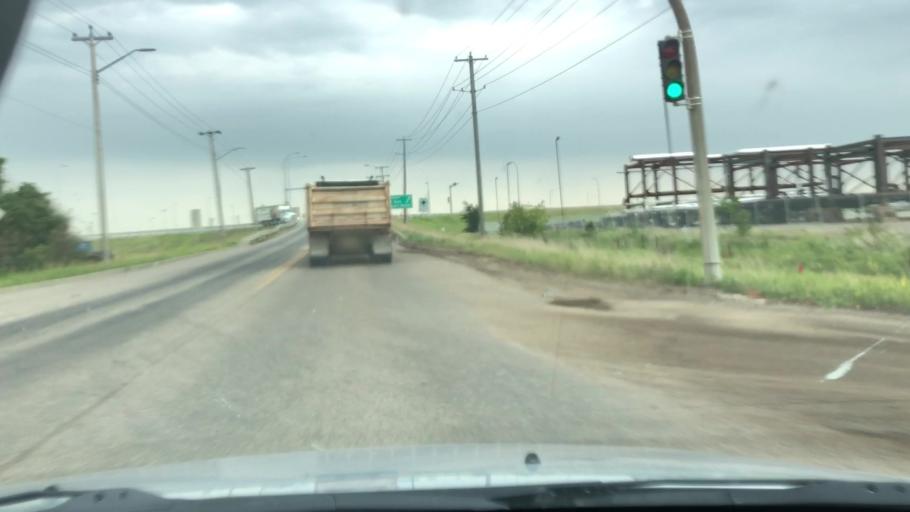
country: CA
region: Alberta
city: Sherwood Park
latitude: 53.5193
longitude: -113.3939
